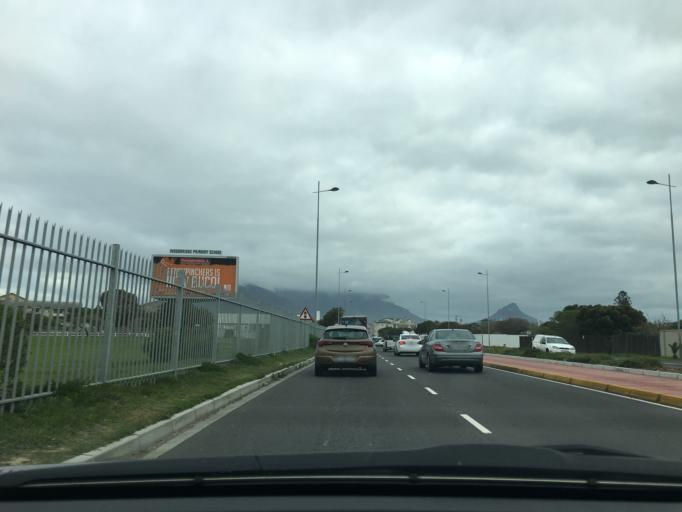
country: ZA
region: Western Cape
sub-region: City of Cape Town
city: Sunset Beach
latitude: -33.8887
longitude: 18.4886
